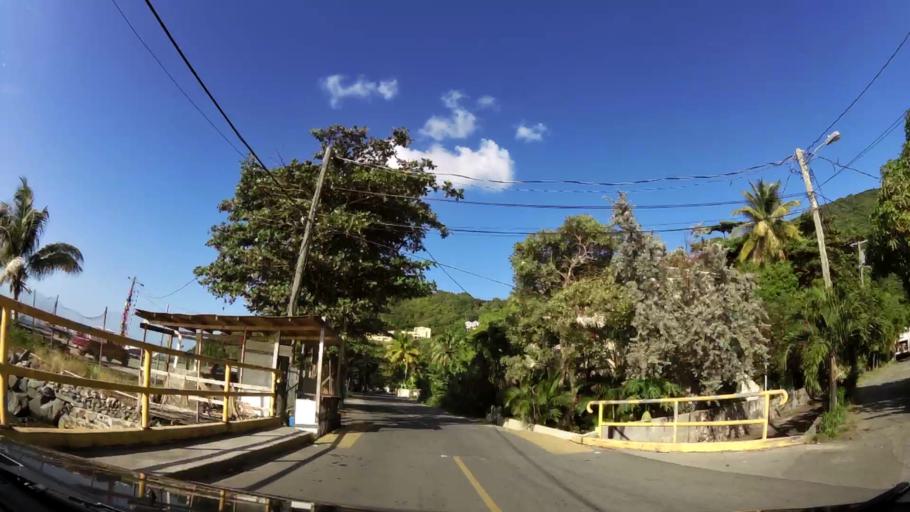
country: VG
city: Road Town
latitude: 18.4117
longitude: -64.6711
